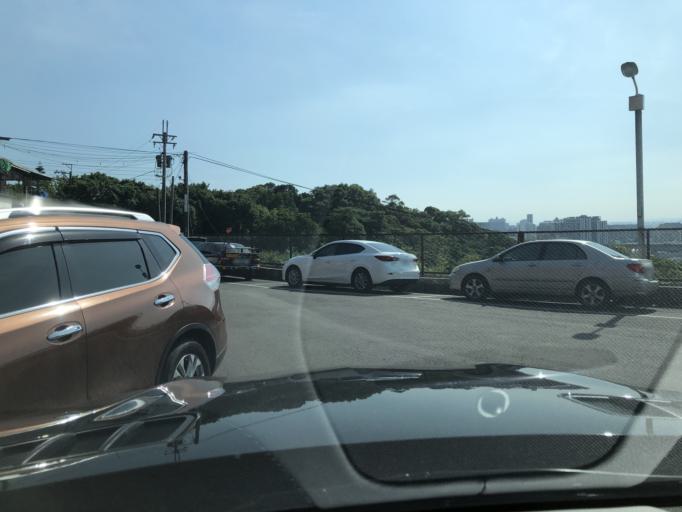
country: TW
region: Taiwan
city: Taoyuan City
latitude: 25.0656
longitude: 121.2936
